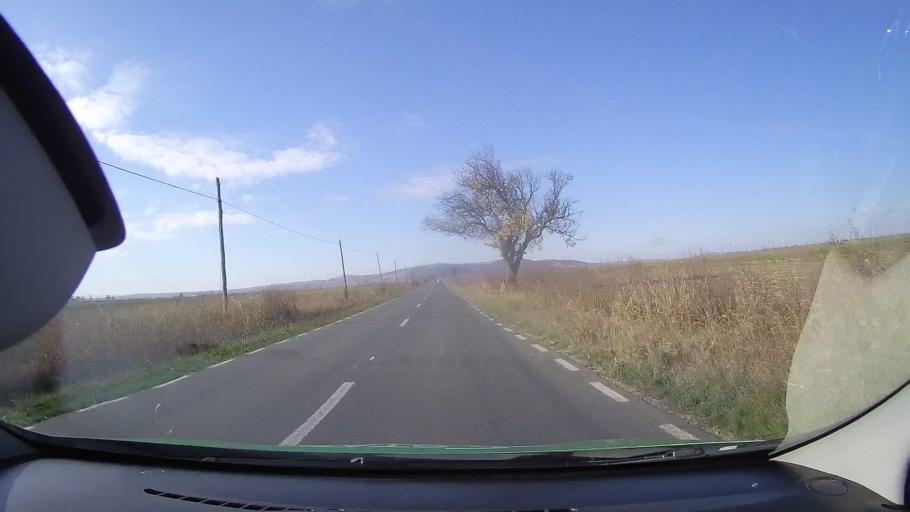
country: RO
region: Tulcea
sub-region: Comuna Valea Nucarilor
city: Valea Nucarilor
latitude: 45.0389
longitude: 28.9147
